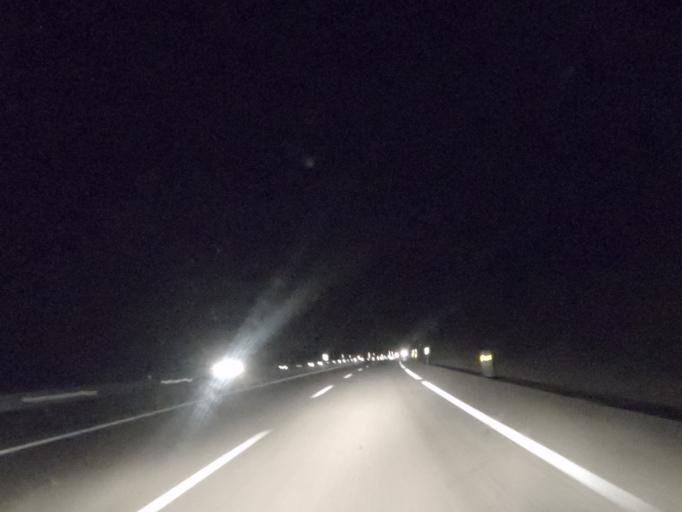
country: ES
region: Castille and Leon
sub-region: Provincia de Zamora
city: Mombuey
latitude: 42.0179
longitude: -6.3399
